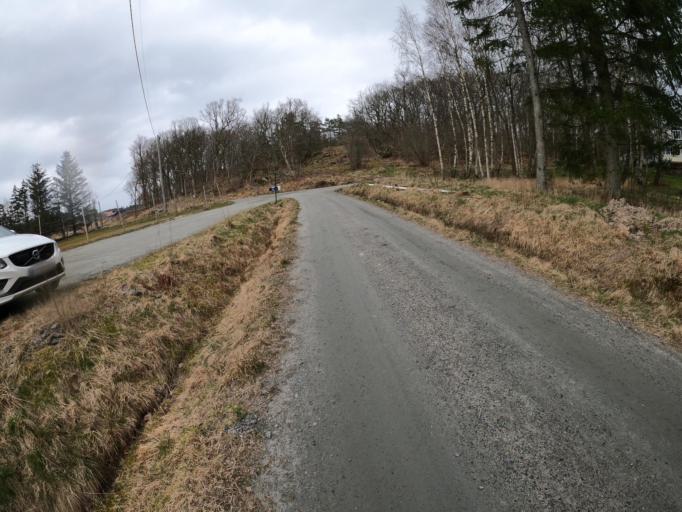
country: SE
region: Vaestra Goetaland
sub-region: Harryda Kommun
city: Molnlycke
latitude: 57.6268
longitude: 12.1081
